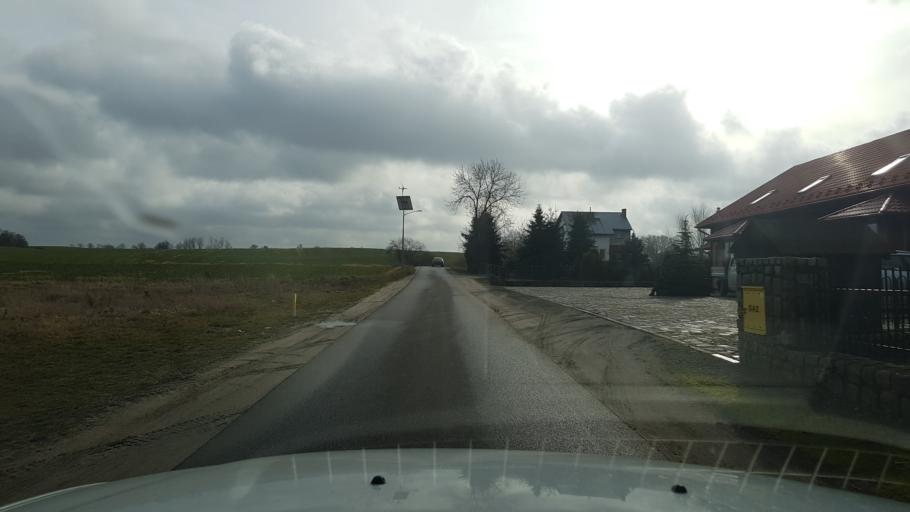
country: PL
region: West Pomeranian Voivodeship
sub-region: Powiat szczecinecki
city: Szczecinek
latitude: 53.7173
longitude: 16.7452
